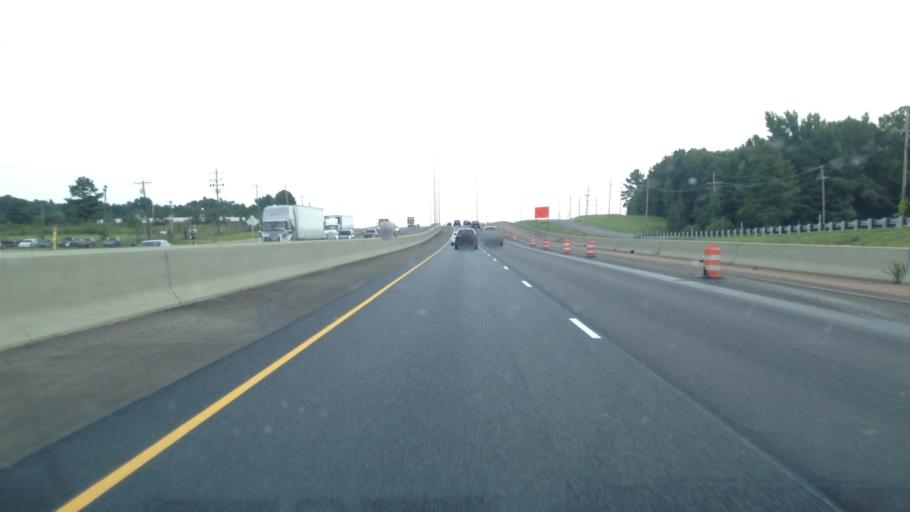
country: US
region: Mississippi
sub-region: Hinds County
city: Byram
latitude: 32.1763
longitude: -90.2618
